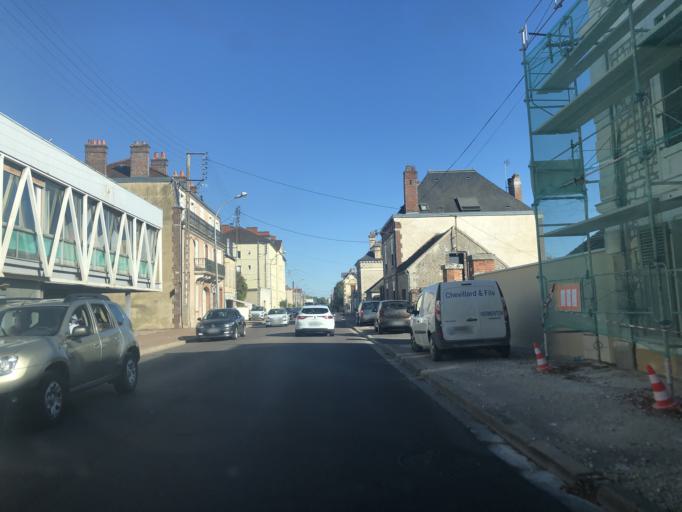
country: FR
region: Bourgogne
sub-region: Departement de l'Yonne
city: Joigny
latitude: 47.9803
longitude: 3.4019
